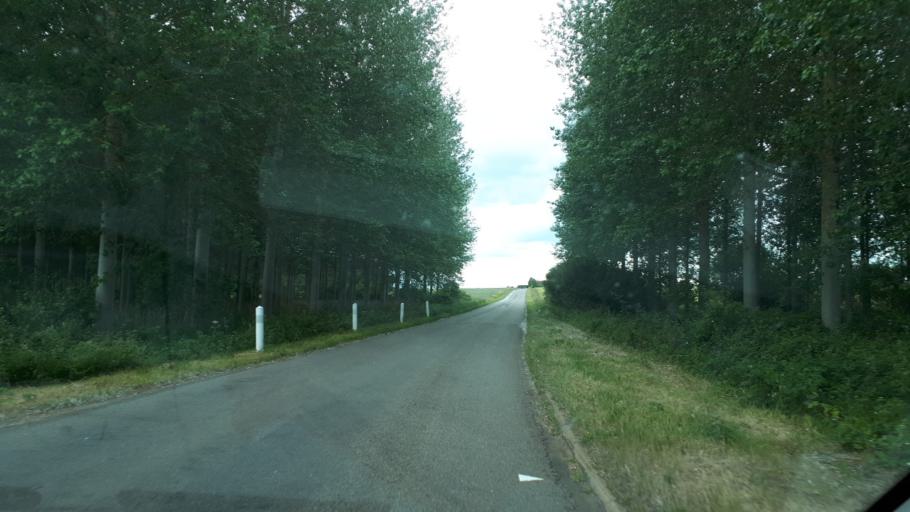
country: FR
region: Centre
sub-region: Departement du Cher
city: Massay
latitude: 47.0969
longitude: 1.9838
